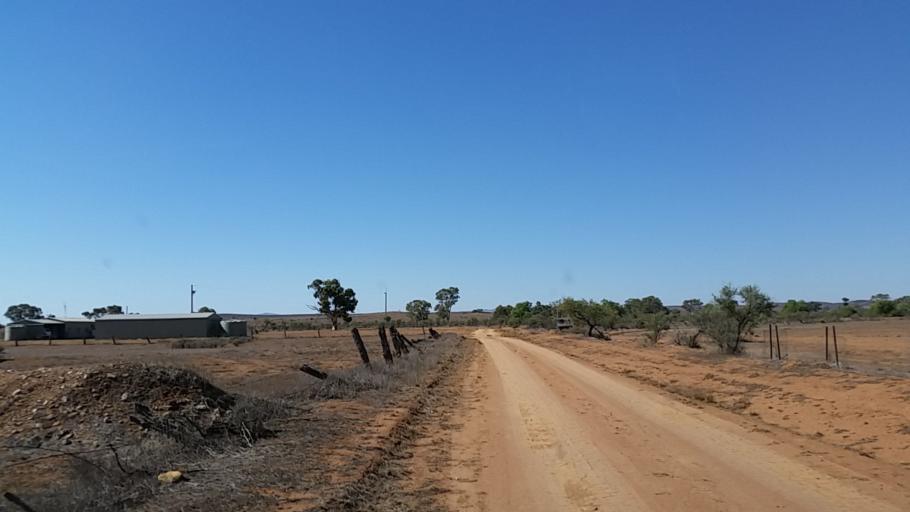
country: AU
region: South Australia
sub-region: Flinders Ranges
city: Quorn
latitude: -32.0727
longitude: 138.4963
